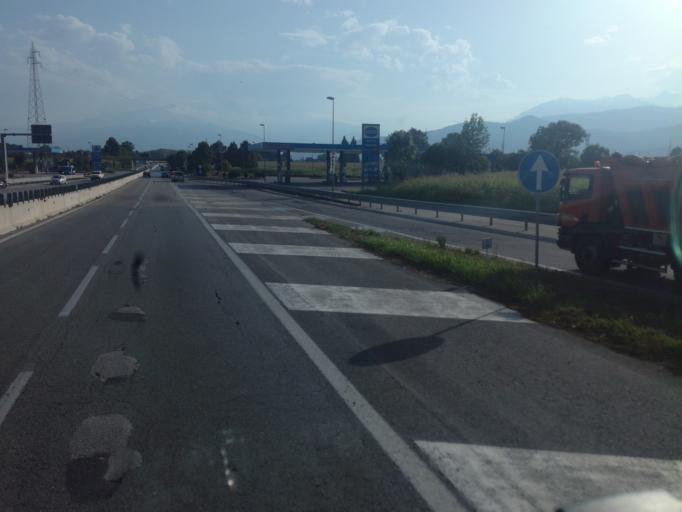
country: IT
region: Piedmont
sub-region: Provincia di Torino
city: Pinerolo
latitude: 44.8777
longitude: 7.3541
